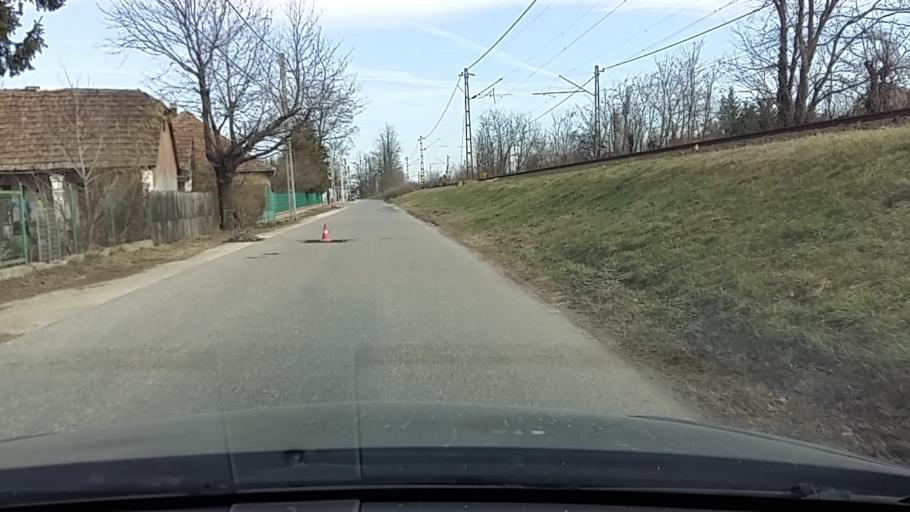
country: HU
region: Pest
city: Szigetszentmiklos
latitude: 47.3509
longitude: 19.0597
